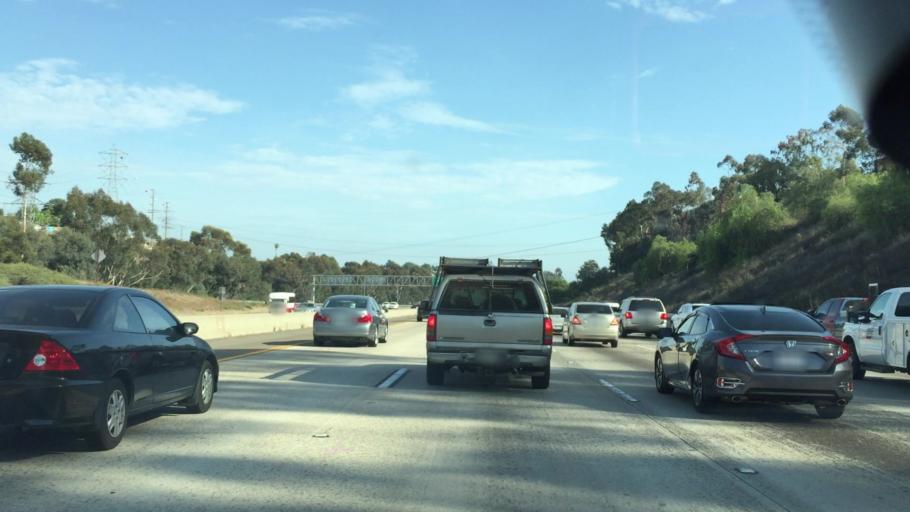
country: US
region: California
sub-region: San Diego County
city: San Diego
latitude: 32.8022
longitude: -117.1504
